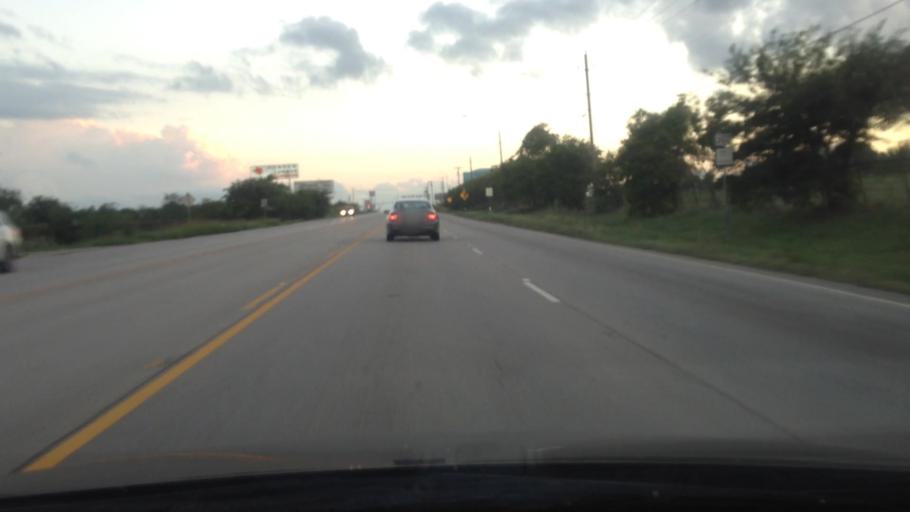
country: US
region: Texas
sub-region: Johnson County
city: Godley
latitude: 32.5363
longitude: -97.6146
